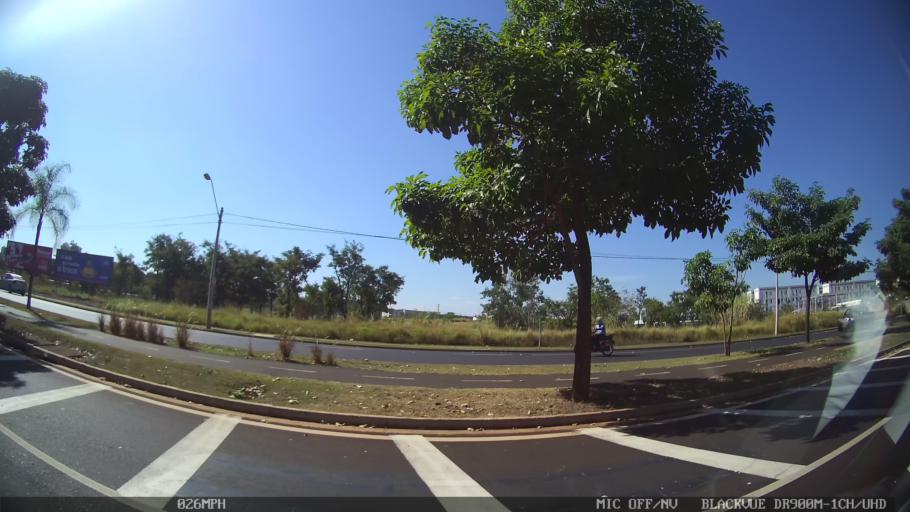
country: BR
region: Sao Paulo
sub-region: Ribeirao Preto
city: Ribeirao Preto
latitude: -21.2116
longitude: -47.7675
